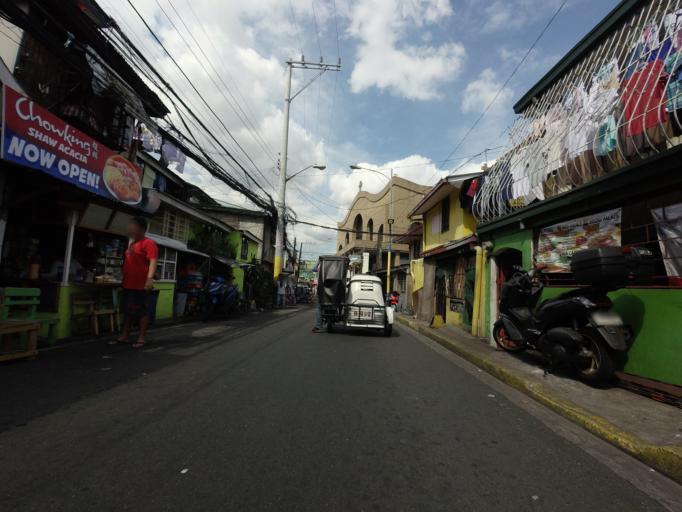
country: PH
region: Metro Manila
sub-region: San Juan
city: San Juan
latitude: 14.5901
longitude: 121.0278
